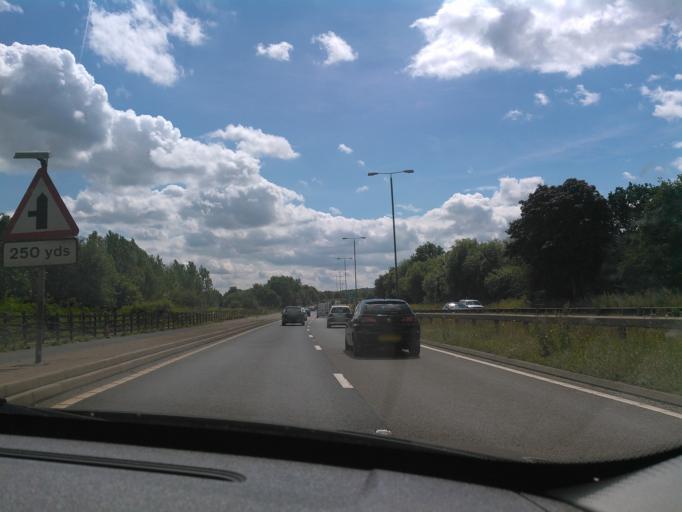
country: GB
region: England
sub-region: Leicestershire
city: Kegworth
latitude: 52.8523
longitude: -1.2988
